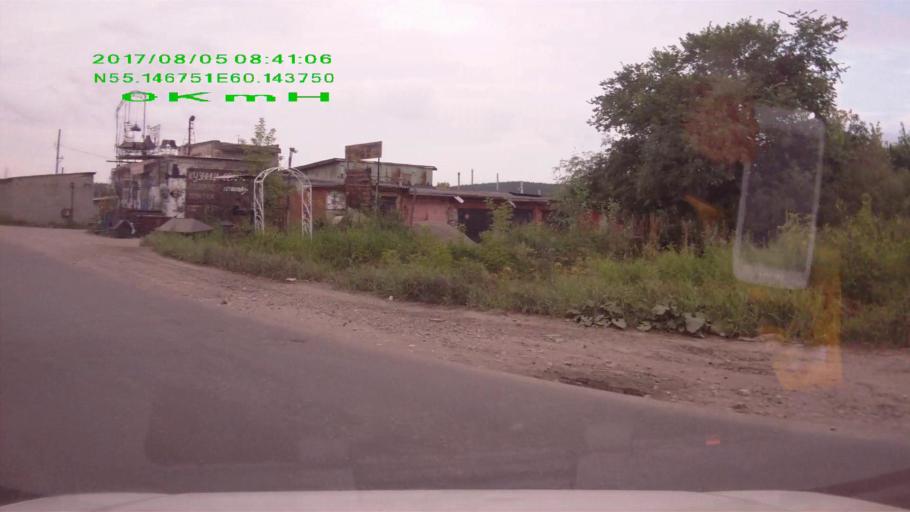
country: RU
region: Chelyabinsk
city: Turgoyak
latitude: 55.1468
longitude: 60.1437
